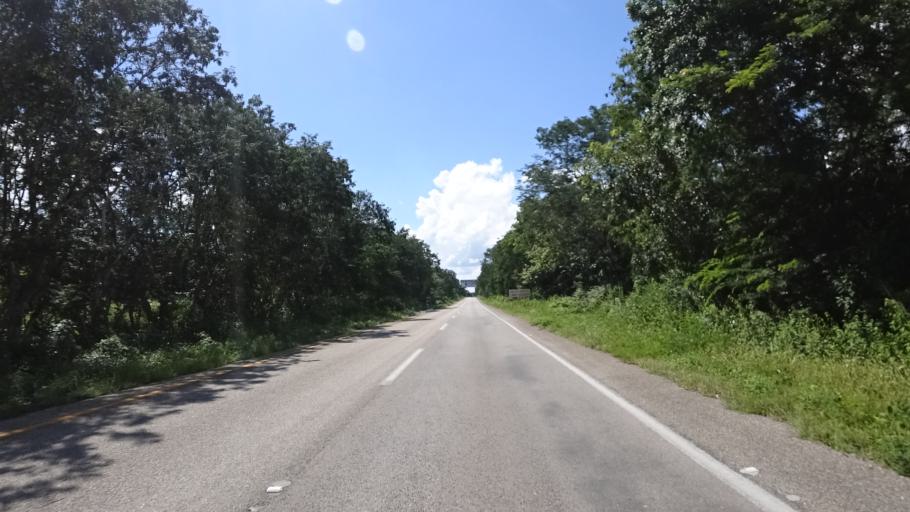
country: MX
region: Yucatan
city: Valladolid
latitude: 20.7432
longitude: -88.2202
